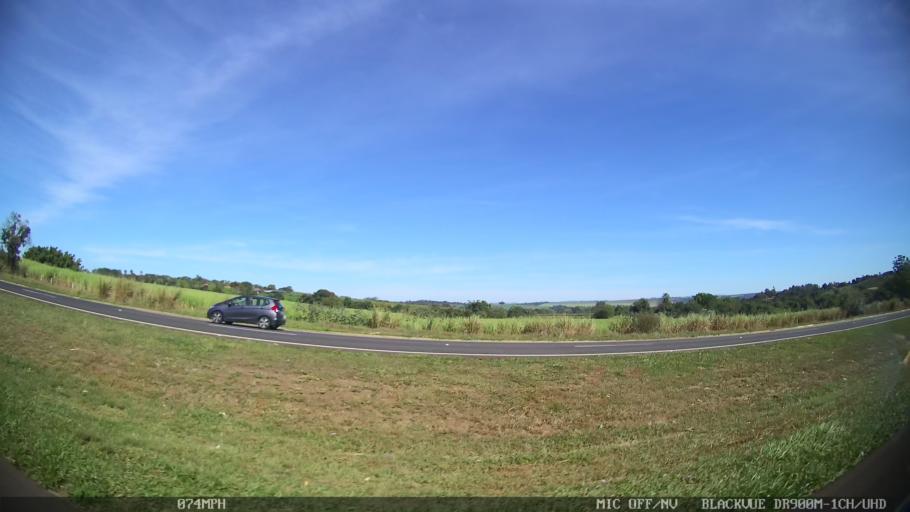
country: BR
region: Sao Paulo
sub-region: Porto Ferreira
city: Porto Ferreira
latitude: -21.7924
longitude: -47.5171
